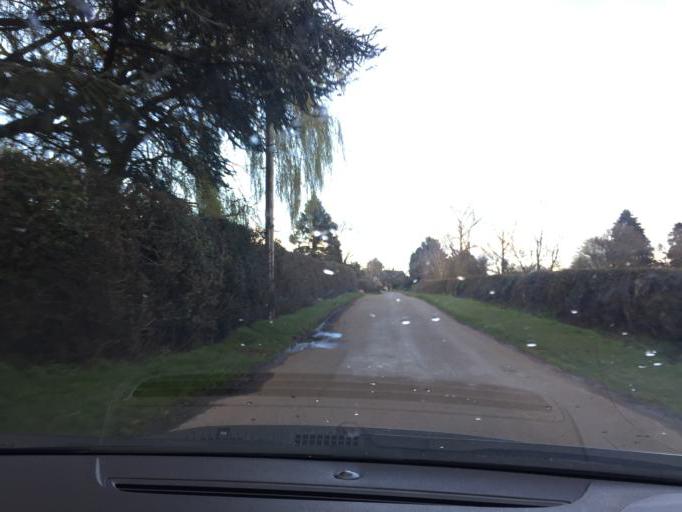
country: GB
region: England
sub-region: Warwickshire
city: Henley in Arden
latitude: 52.2764
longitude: -1.7205
